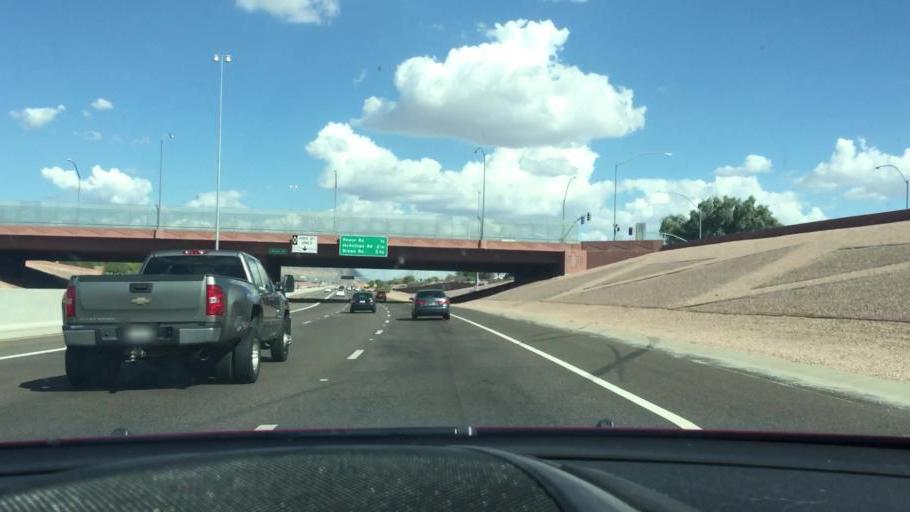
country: US
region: Arizona
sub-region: Maricopa County
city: Mesa
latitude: 33.4745
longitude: -111.7027
